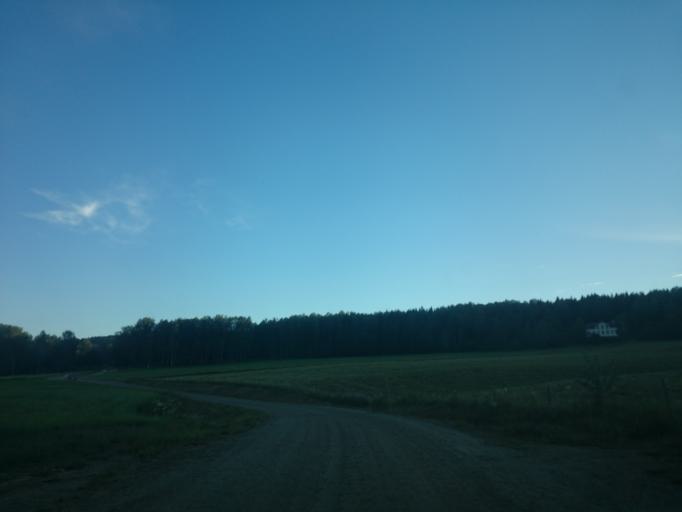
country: SE
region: Vaesternorrland
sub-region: Kramfors Kommun
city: Bollstabruk
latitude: 63.0561
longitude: 17.7293
